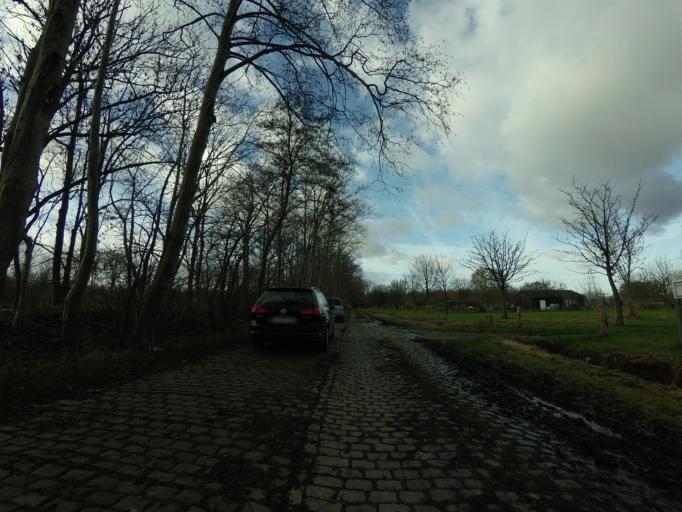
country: BE
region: Flanders
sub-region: Provincie Antwerpen
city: Stabroek
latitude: 51.2847
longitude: 4.3921
